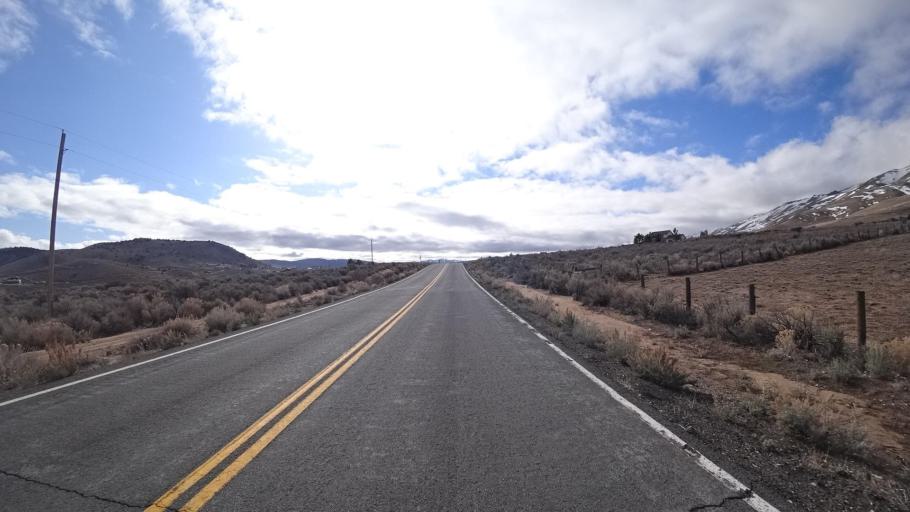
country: US
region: Nevada
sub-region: Washoe County
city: Cold Springs
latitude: 39.8862
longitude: -119.9714
